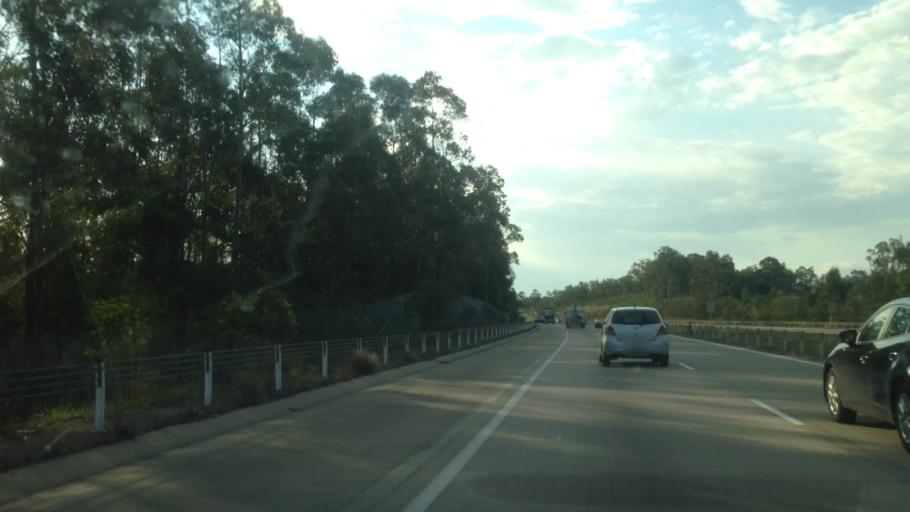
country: AU
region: New South Wales
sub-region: Cessnock
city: Heddon Greta
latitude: -32.8348
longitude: 151.5376
